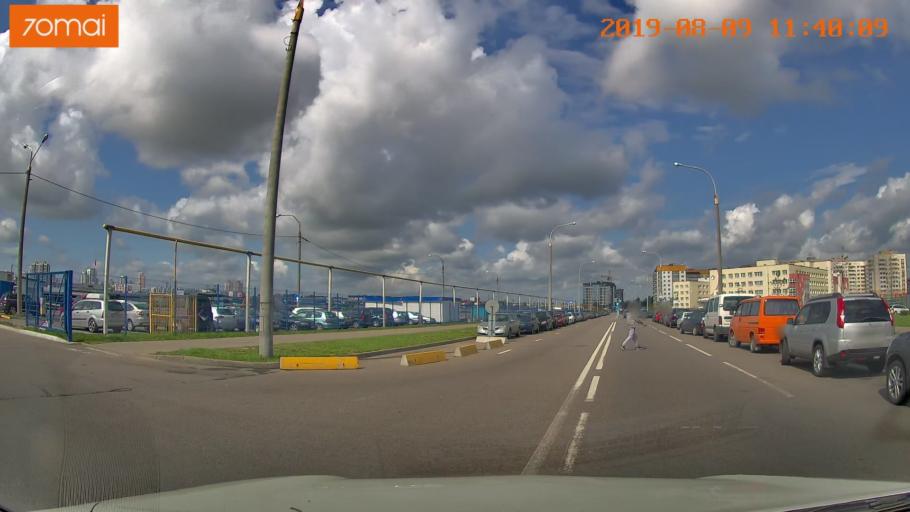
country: BY
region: Minsk
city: Zhdanovichy
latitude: 53.9355
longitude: 27.4584
